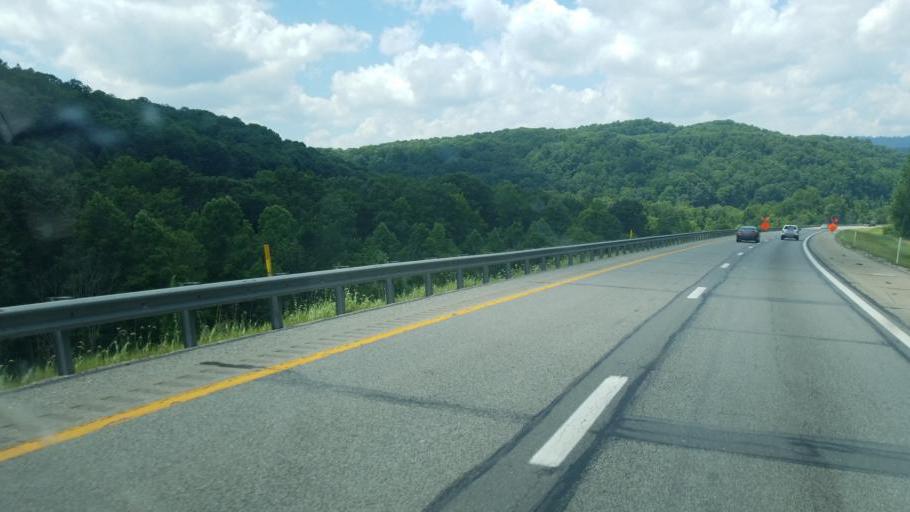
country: US
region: West Virginia
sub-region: Raleigh County
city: Prosperity
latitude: 37.8487
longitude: -81.2466
